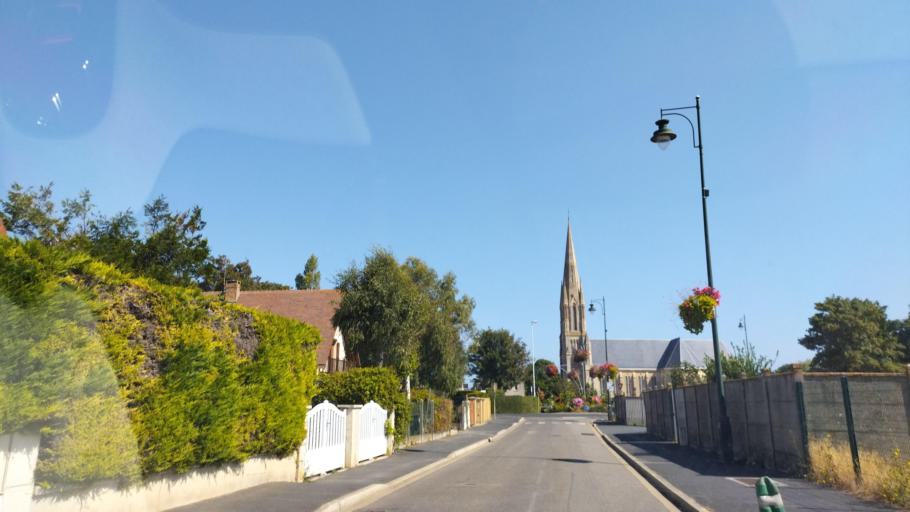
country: FR
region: Lower Normandy
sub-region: Departement du Calvados
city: Saint-Aubin-sur-Mer
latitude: 49.3272
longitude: -0.3966
